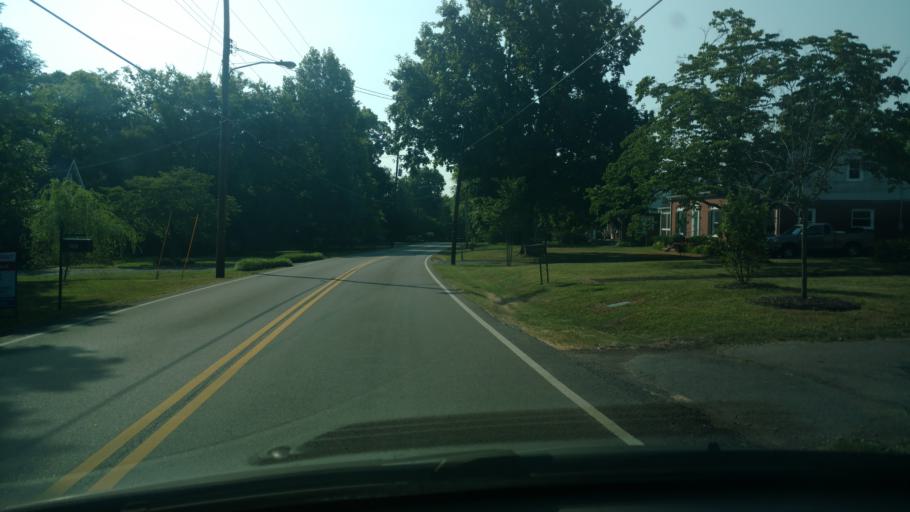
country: US
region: Tennessee
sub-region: Davidson County
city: Lakewood
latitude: 36.2199
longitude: -86.7140
